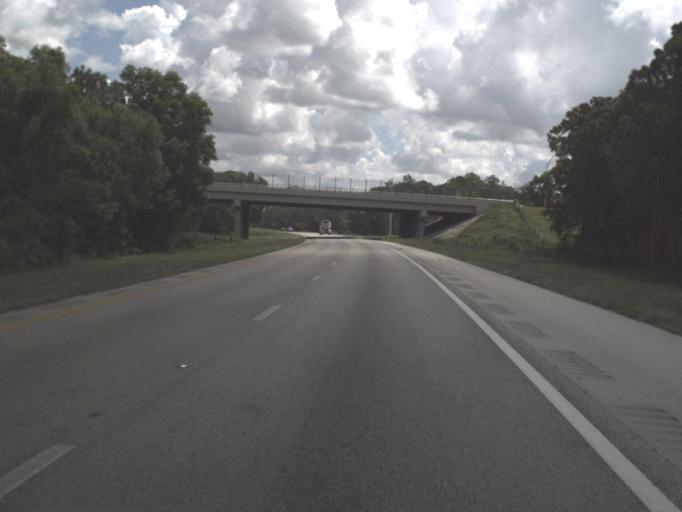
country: US
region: Florida
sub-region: Collier County
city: Golden Gate
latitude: 26.1634
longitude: -81.7205
